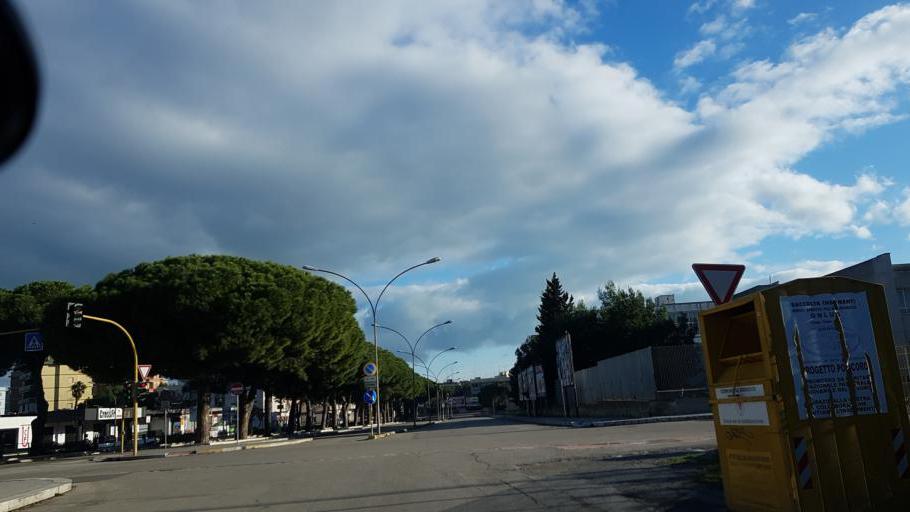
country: IT
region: Apulia
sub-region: Provincia di Brindisi
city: Brindisi
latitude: 40.6230
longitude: 17.9258
